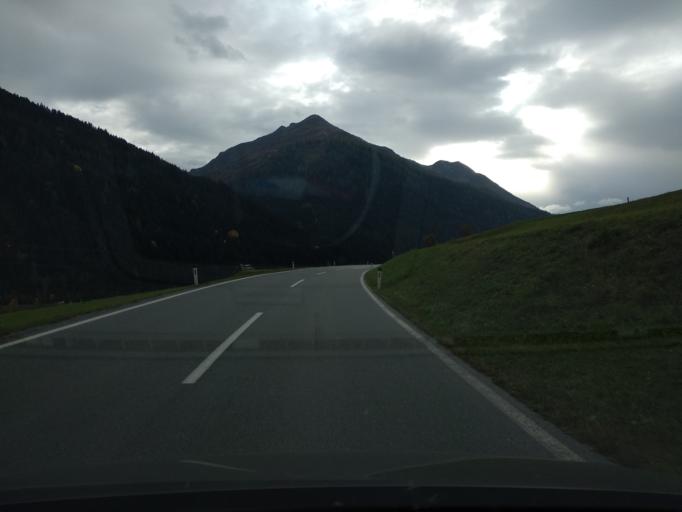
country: AT
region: Tyrol
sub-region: Politischer Bezirk Landeck
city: Flirsch
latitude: 47.1513
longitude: 10.3545
